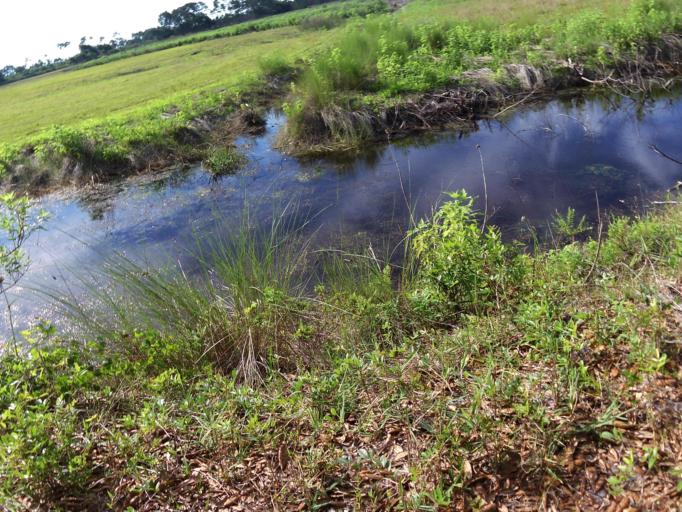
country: US
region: Florida
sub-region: Saint Johns County
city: Villano Beach
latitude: 30.0263
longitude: -81.3373
